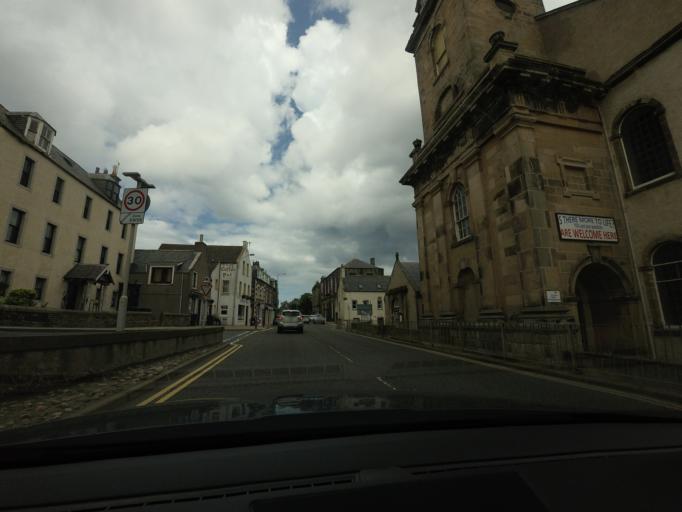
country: GB
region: Scotland
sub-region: Aberdeenshire
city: Banff
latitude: 57.6629
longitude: -2.5234
